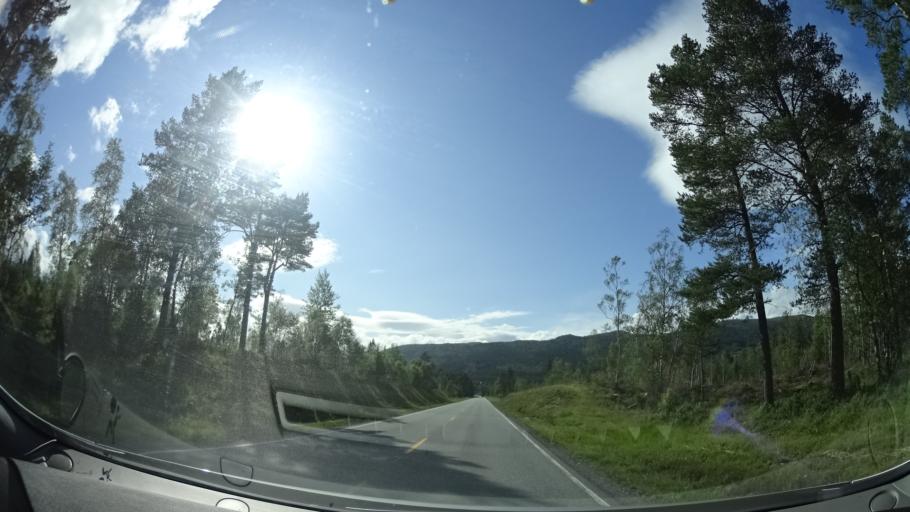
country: NO
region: Sor-Trondelag
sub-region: Hemne
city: Kyrksaeterora
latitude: 63.2100
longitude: 9.0351
